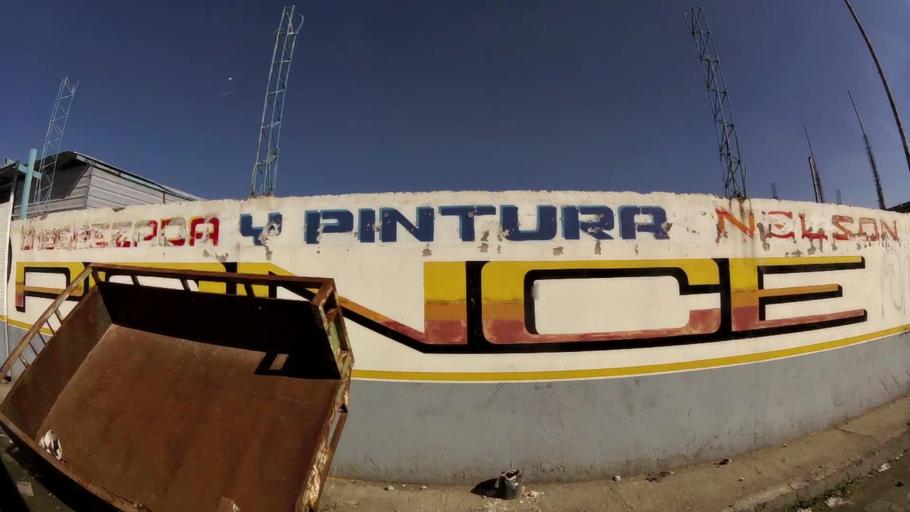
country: EC
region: Chimborazo
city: Riobamba
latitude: -1.6500
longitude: -78.6723
